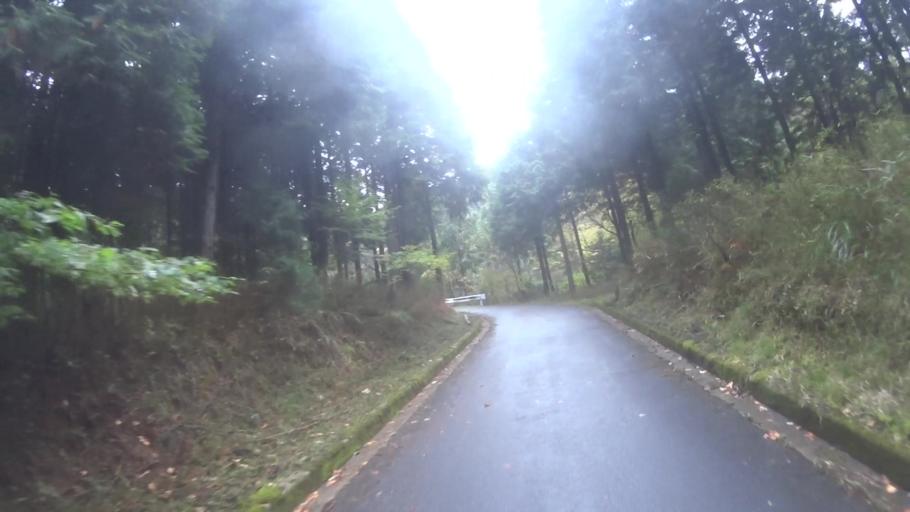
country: JP
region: Kyoto
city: Miyazu
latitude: 35.4885
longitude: 135.1259
